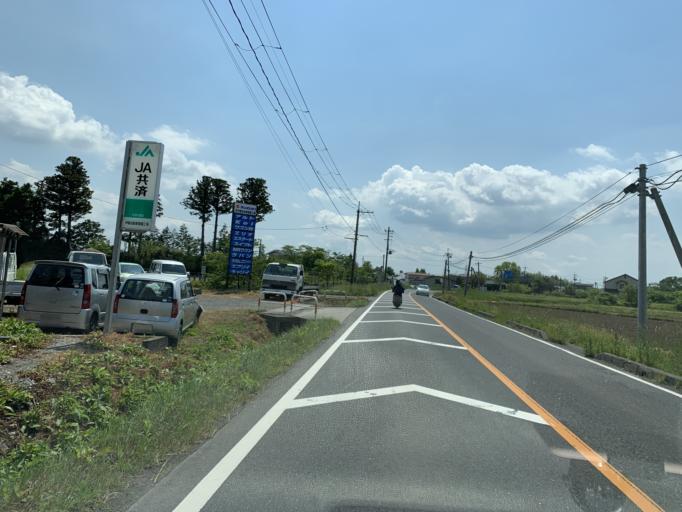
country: JP
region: Miyagi
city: Kogota
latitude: 38.5673
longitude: 141.0449
